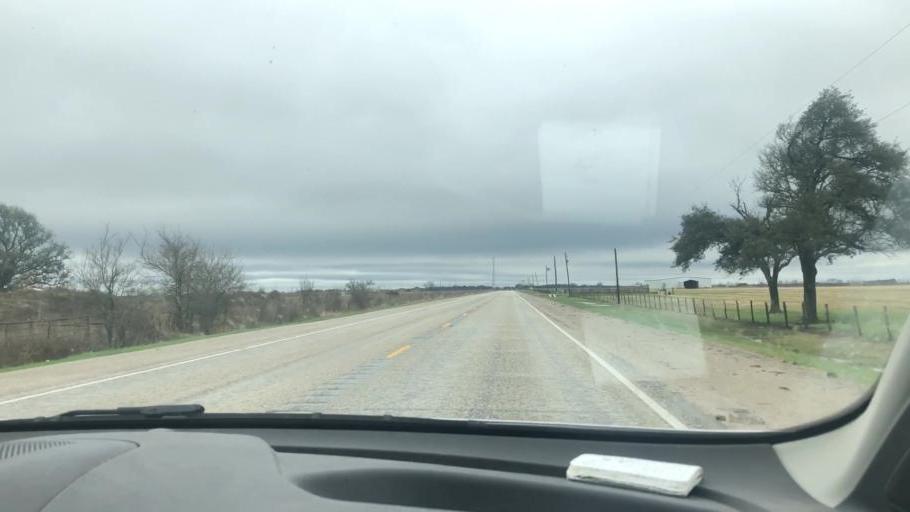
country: US
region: Texas
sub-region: Wharton County
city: Wharton
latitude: 29.2447
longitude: -96.0445
